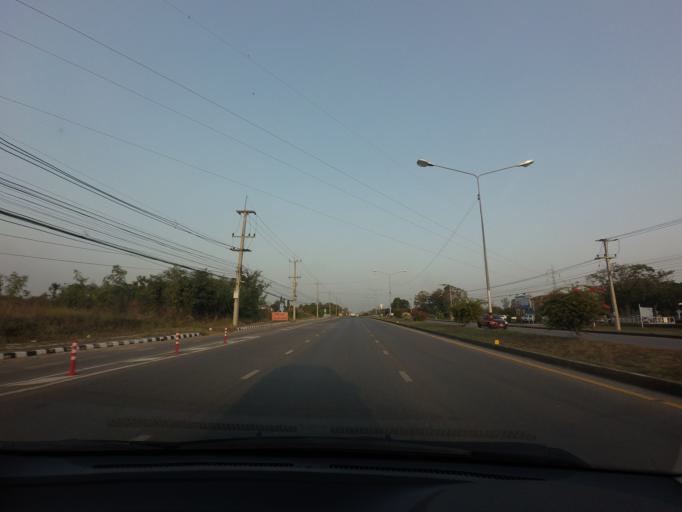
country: TH
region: Sukhothai
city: Sukhothai
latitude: 17.0206
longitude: 99.8632
